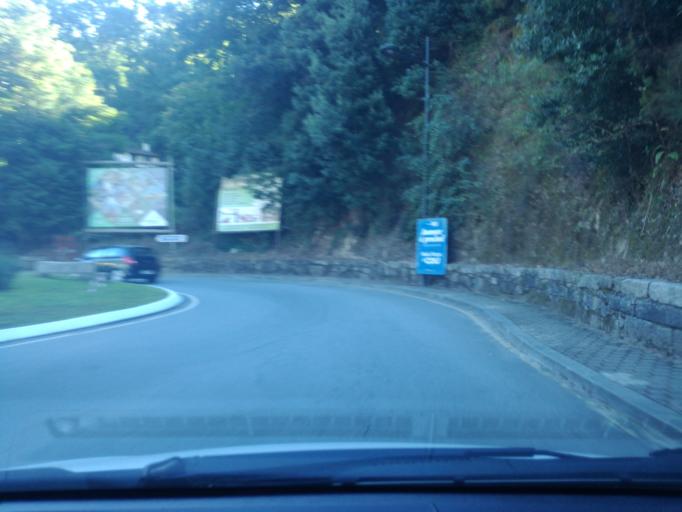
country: PT
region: Braga
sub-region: Vieira do Minho
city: Real
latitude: 41.7243
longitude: -8.1627
